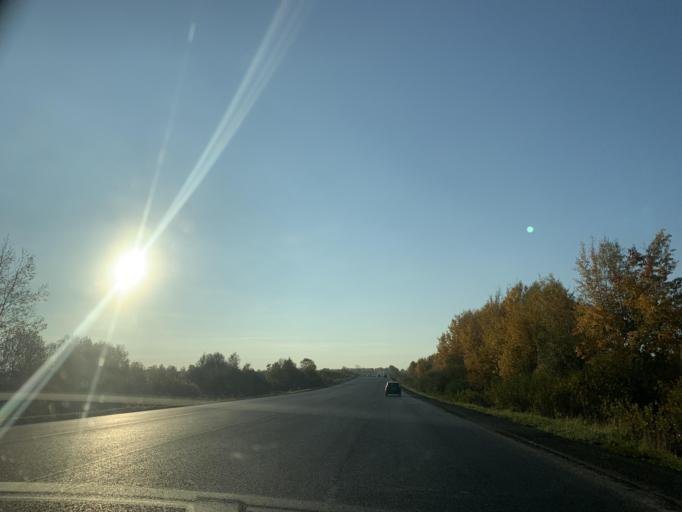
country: RU
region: Jaroslavl
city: Konstantinovskiy
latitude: 57.7995
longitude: 39.5962
